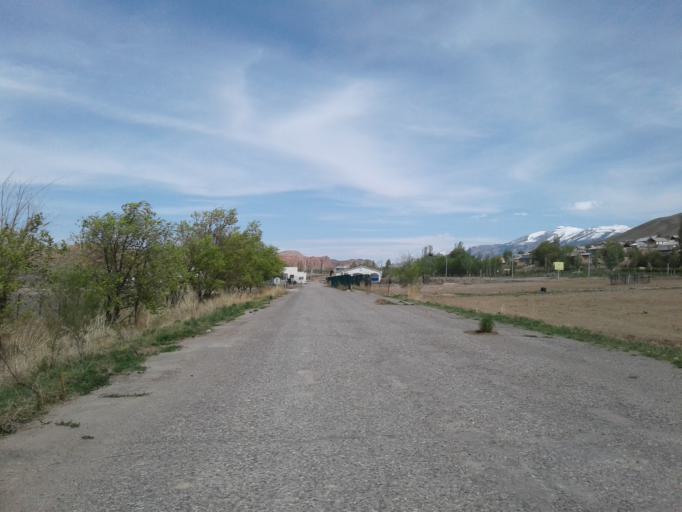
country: KG
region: Naryn
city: Naryn
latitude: 41.4306
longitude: 75.9034
